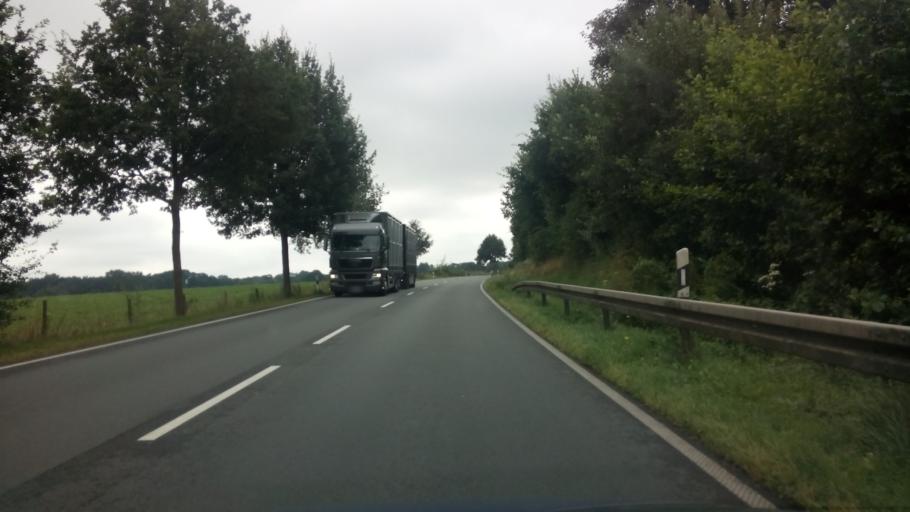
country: DE
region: Lower Saxony
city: Bassum
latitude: 52.8536
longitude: 8.7533
